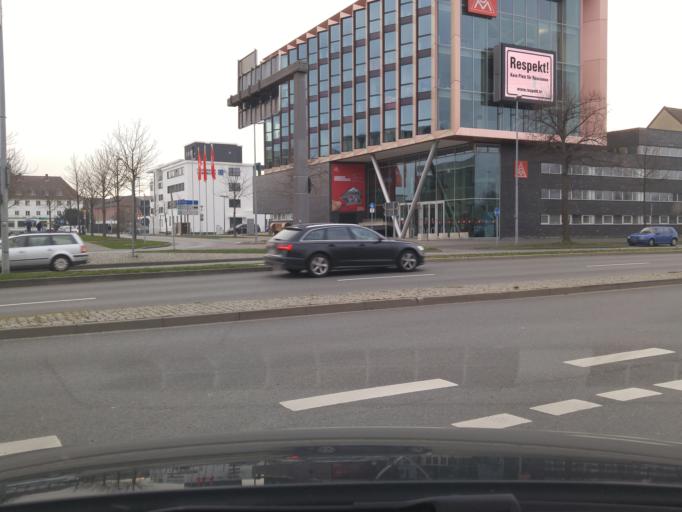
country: DE
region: Lower Saxony
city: Wolfsburg
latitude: 52.4281
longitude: 10.7865
